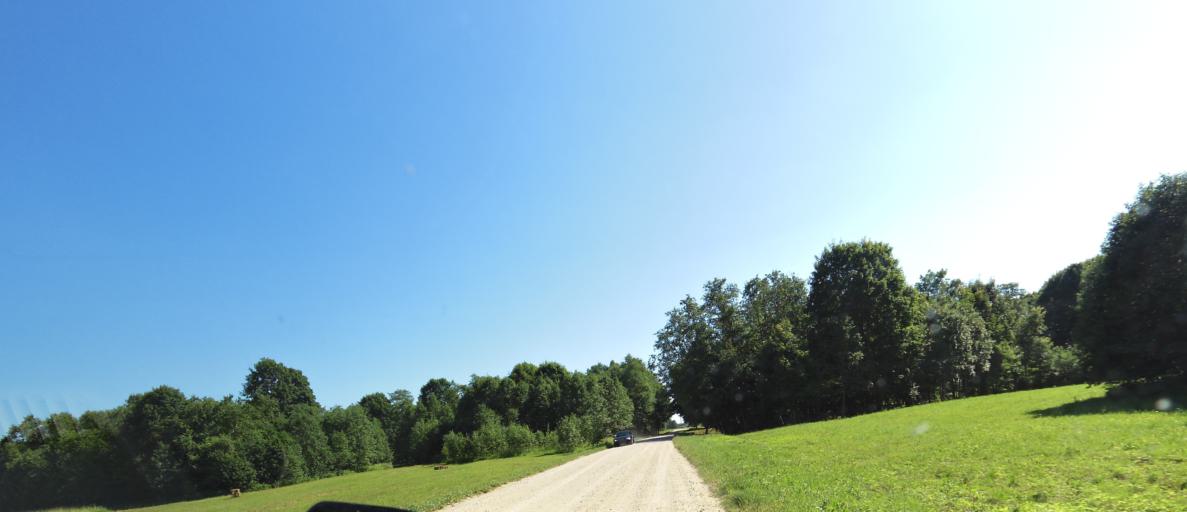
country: LT
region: Panevezys
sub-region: Birzai
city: Birzai
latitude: 56.2085
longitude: 24.6927
